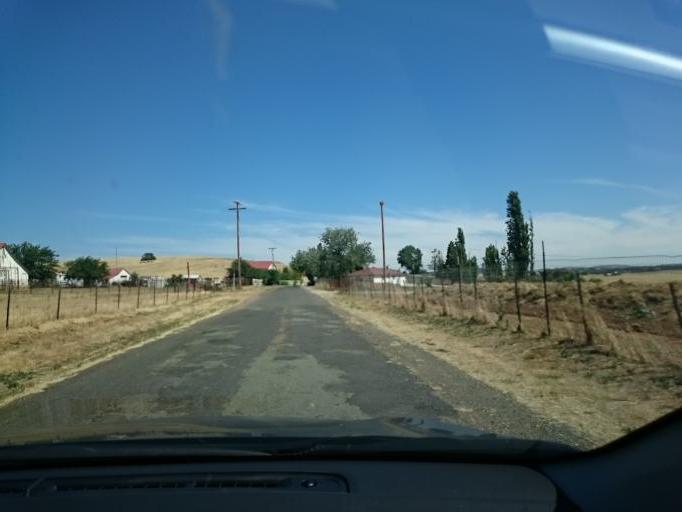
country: US
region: California
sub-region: Calaveras County
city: Copperopolis
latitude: 38.0547
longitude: -120.7250
